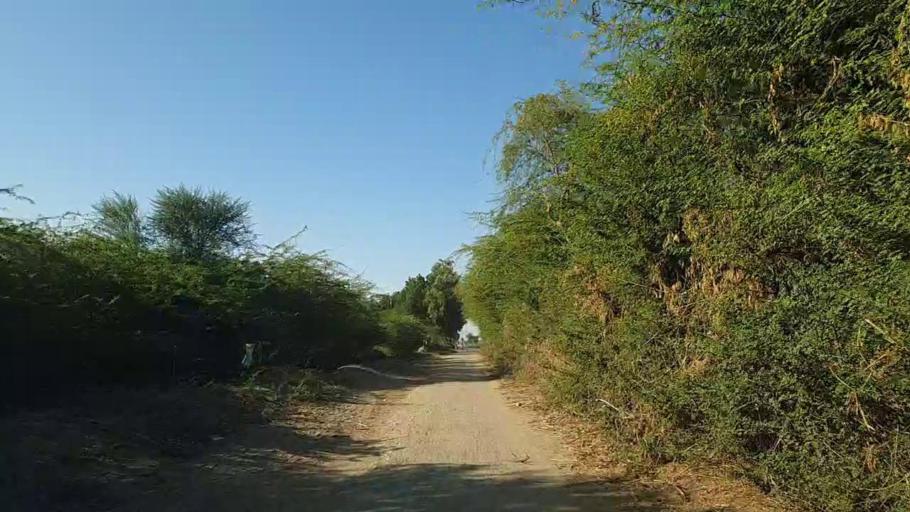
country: PK
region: Sindh
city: Samaro
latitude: 25.2671
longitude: 69.4841
